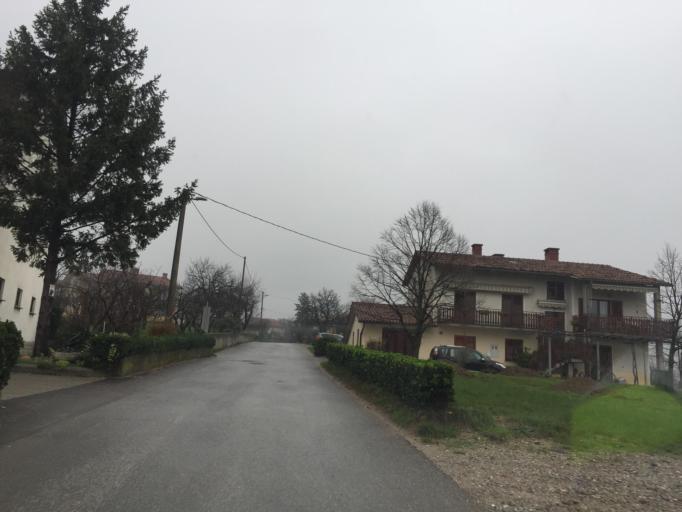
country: SI
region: Ajdovscina
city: Lokavec
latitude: 45.8987
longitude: 13.8765
